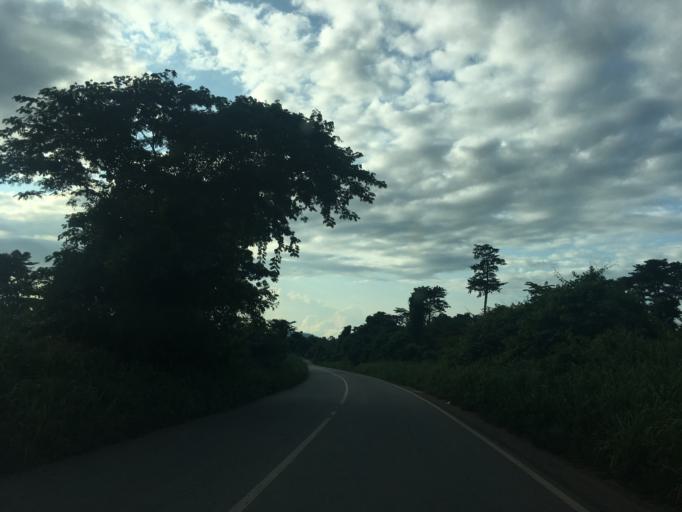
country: GH
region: Western
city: Bibiani
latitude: 6.3501
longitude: -2.2781
